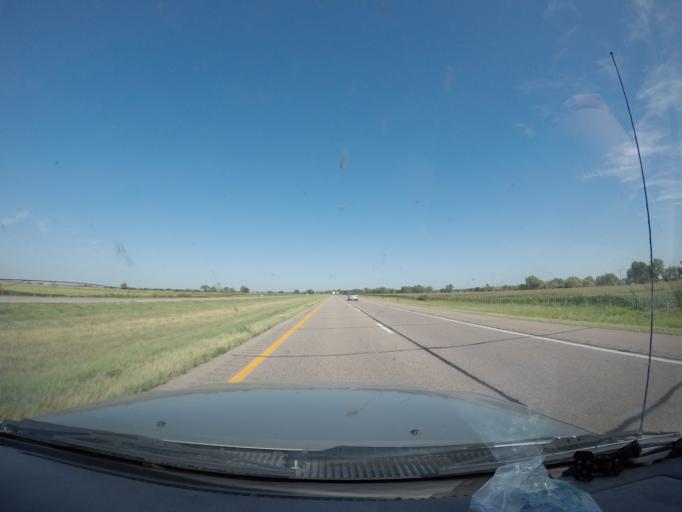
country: US
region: Nebraska
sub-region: Buffalo County
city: Kearney
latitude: 40.6879
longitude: -99.3295
